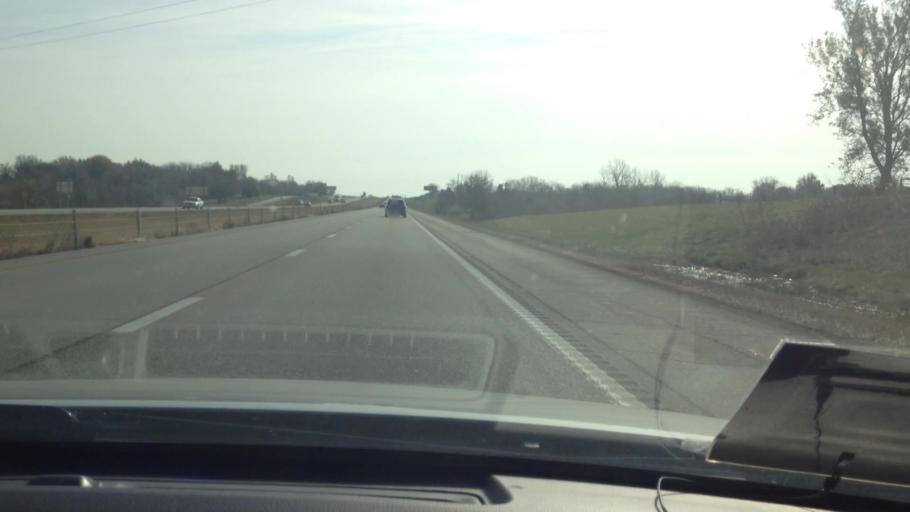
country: US
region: Missouri
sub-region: Cass County
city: Peculiar
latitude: 38.7174
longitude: -94.4499
